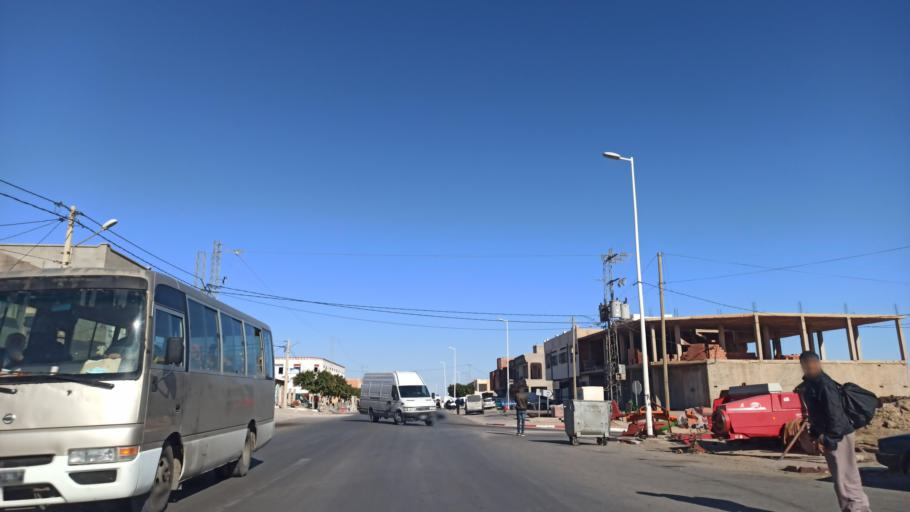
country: TN
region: Sidi Bu Zayd
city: Bi'r al Hufayy
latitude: 34.9390
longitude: 9.2016
